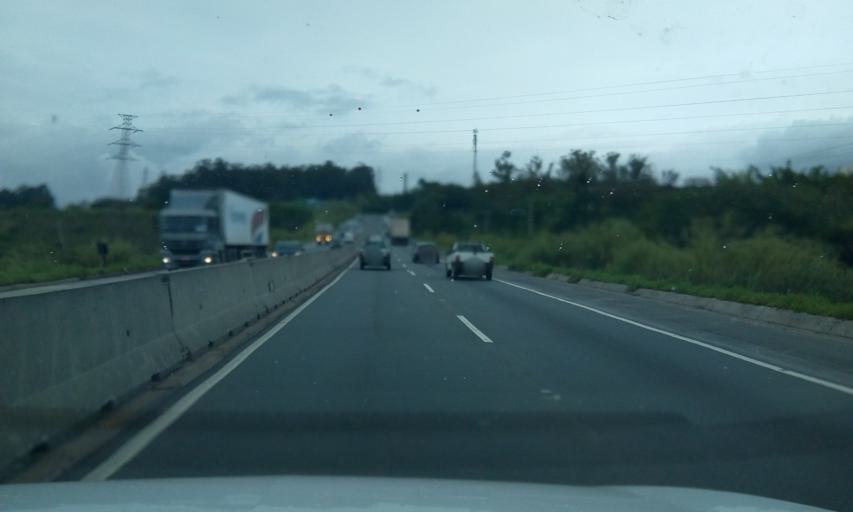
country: BR
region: Sao Paulo
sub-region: Itupeva
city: Itupeva
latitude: -23.1785
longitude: -46.9764
